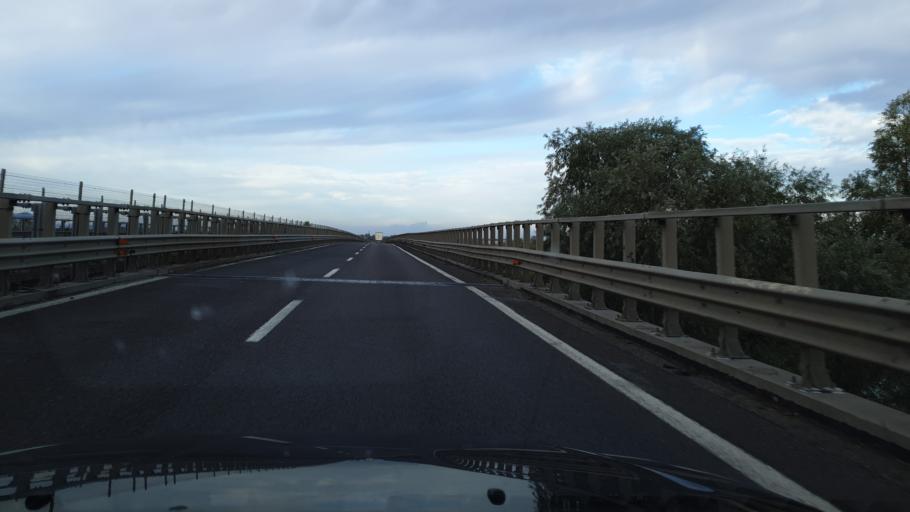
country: IT
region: Veneto
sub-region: Provincia di Padova
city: Boara Pisani
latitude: 45.0963
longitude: 11.7512
